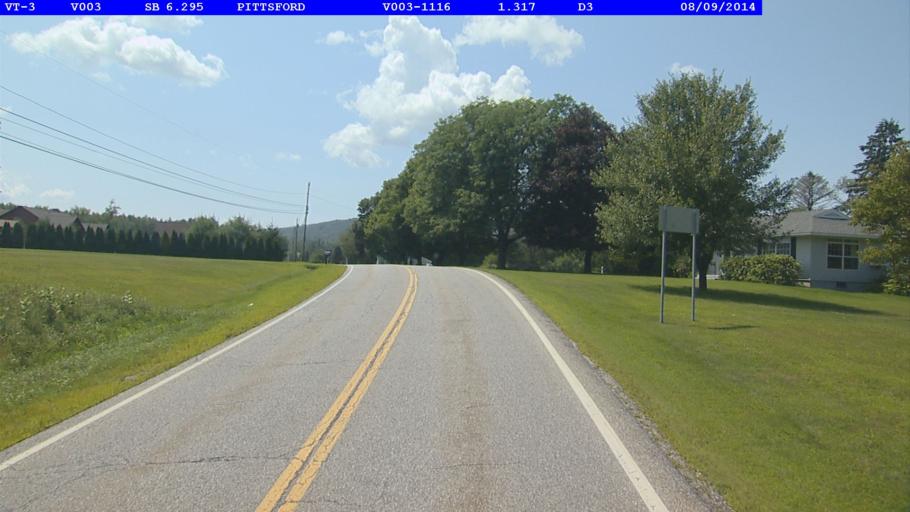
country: US
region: Vermont
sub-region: Rutland County
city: Rutland
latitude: 43.6828
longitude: -73.0236
